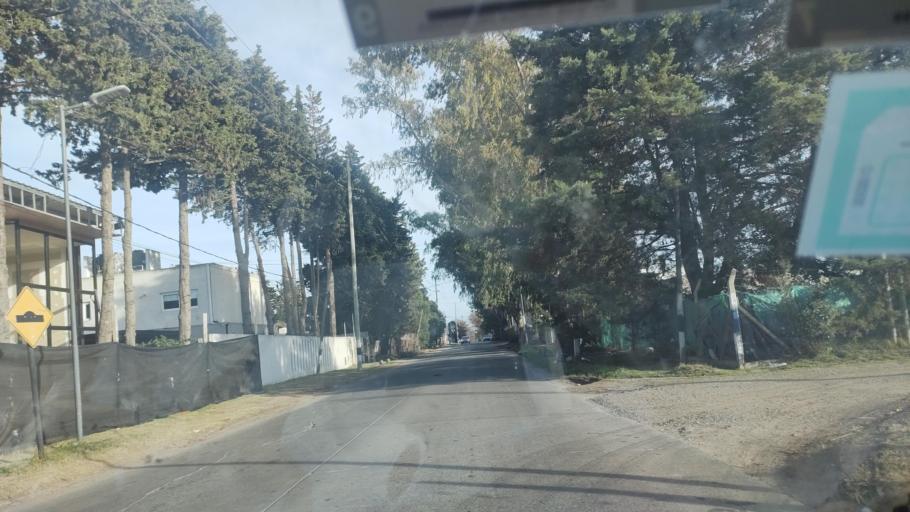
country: AR
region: Buenos Aires
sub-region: Partido de La Plata
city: La Plata
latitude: -34.9002
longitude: -58.0350
